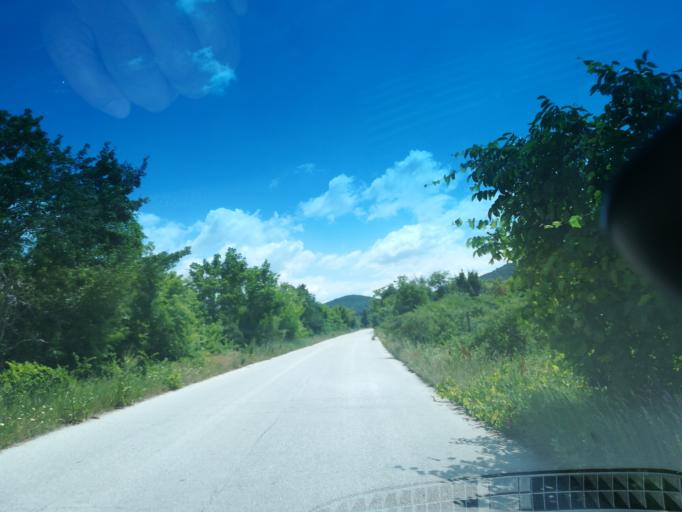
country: BG
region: Khaskovo
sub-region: Obshtina Mineralni Bani
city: Mineralni Bani
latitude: 41.9852
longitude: 25.2459
